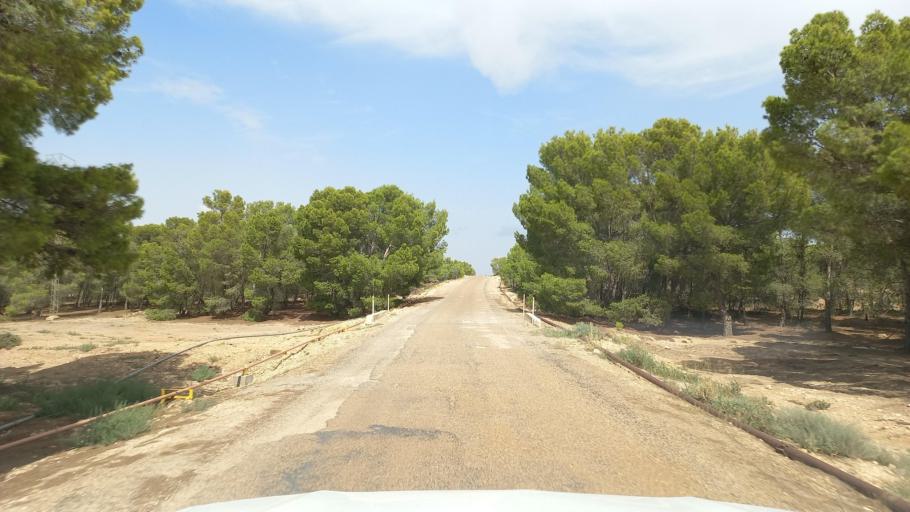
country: TN
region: Al Qasrayn
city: Sbiba
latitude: 35.3892
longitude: 8.9074
